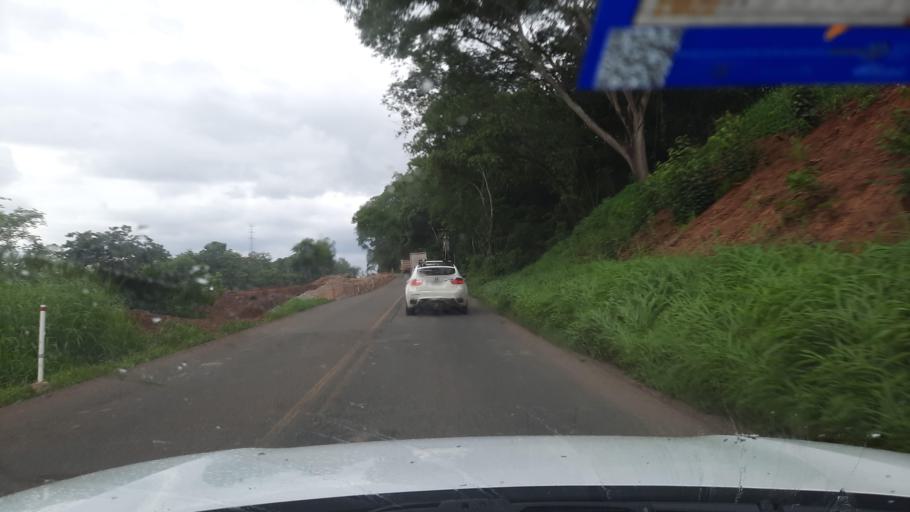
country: CR
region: Puntarenas
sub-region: Canton Central de Puntarenas
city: Puntarenas
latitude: 10.1167
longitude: -84.8955
